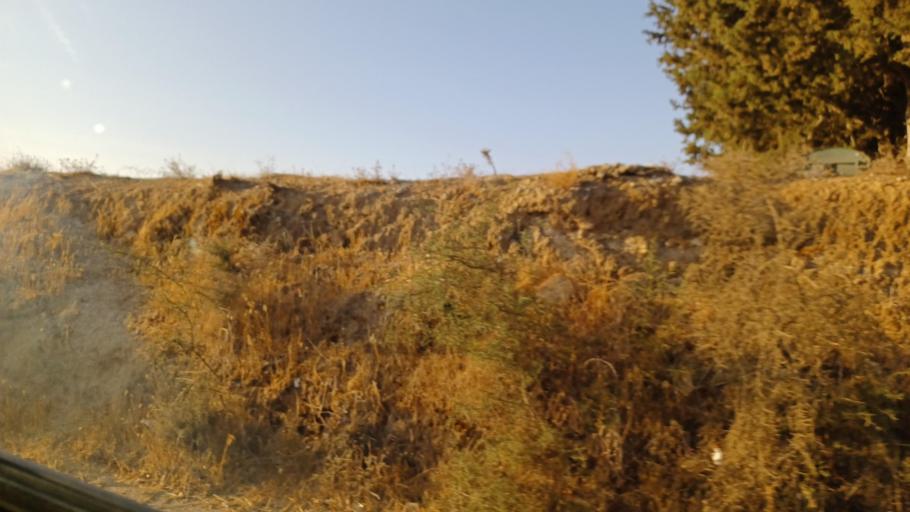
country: CY
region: Pafos
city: Tala
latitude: 34.9213
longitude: 32.5032
